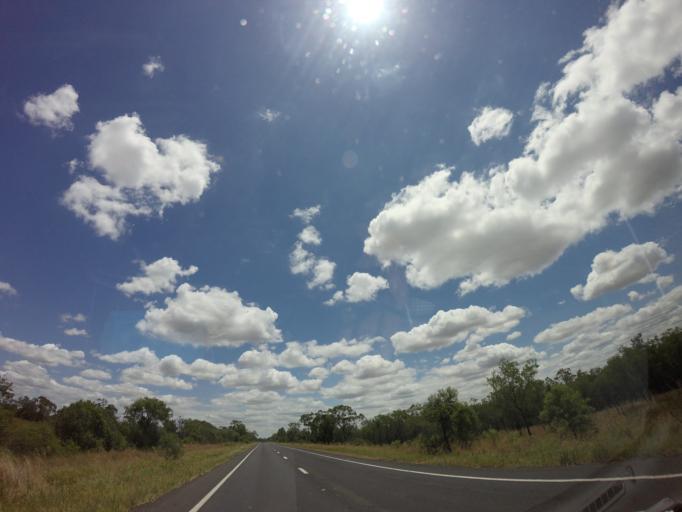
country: AU
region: New South Wales
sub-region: Moree Plains
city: Boggabilla
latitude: -28.7462
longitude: 150.2679
